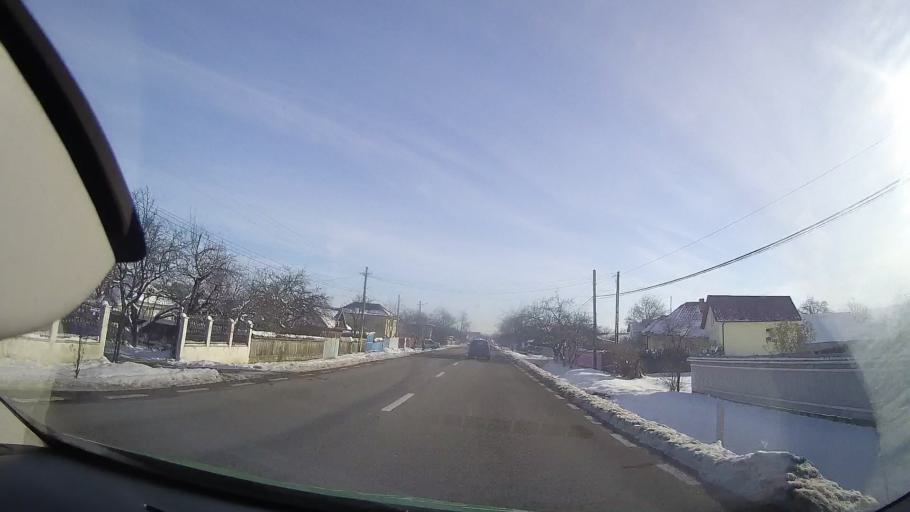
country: RO
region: Neamt
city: Bodesti
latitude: 47.0541
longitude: 26.3978
